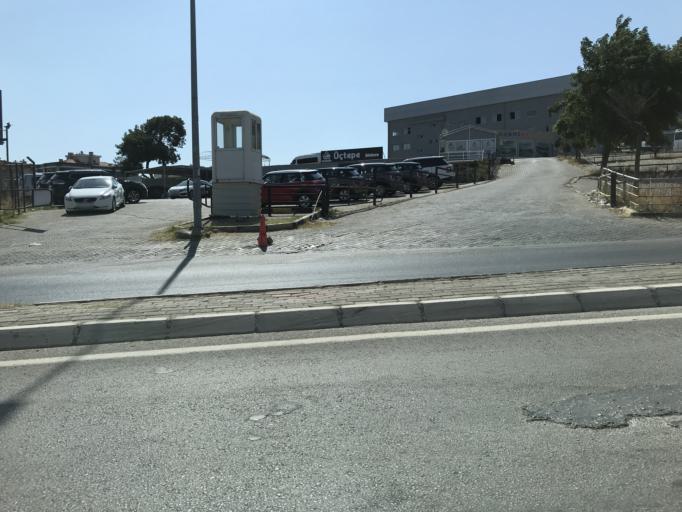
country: TR
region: Izmir
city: Gaziemir
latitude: 38.3409
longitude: 27.1341
